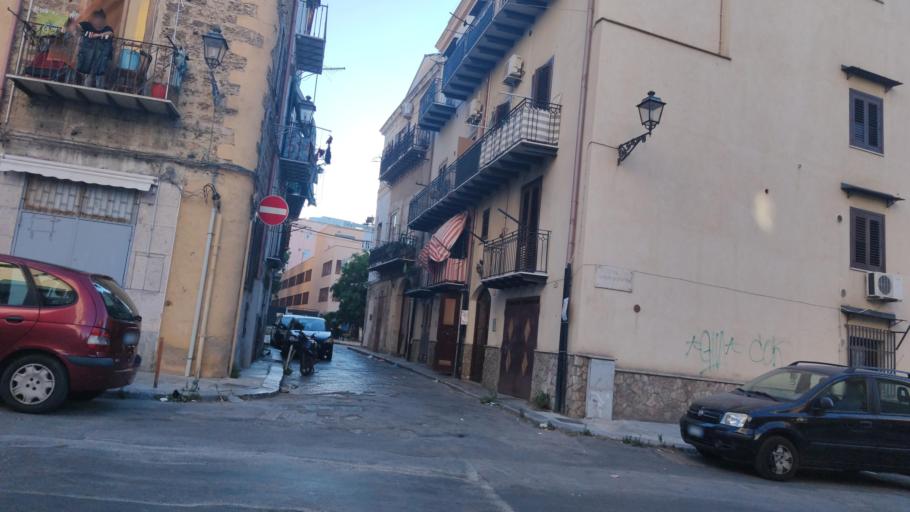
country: IT
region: Sicily
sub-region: Palermo
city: Palermo
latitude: 38.1096
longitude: 13.3575
